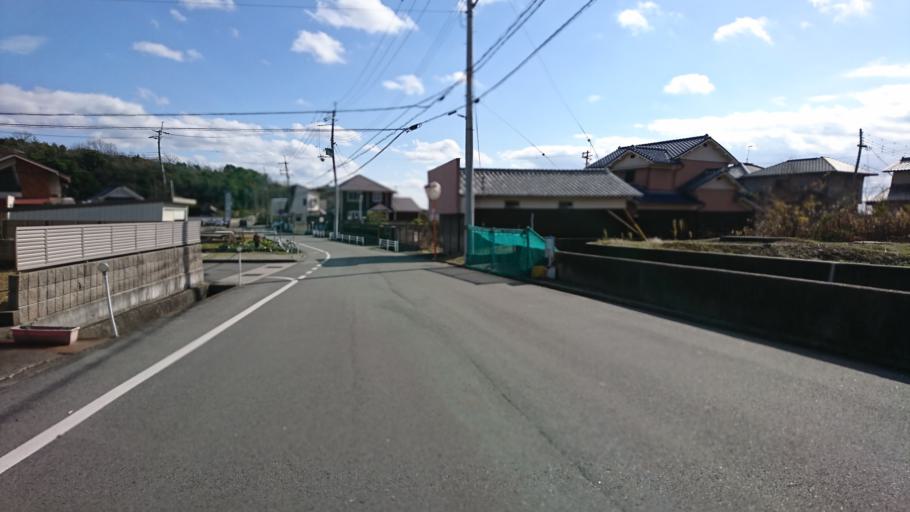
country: JP
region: Hyogo
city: Kakogawacho-honmachi
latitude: 34.8066
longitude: 134.7782
